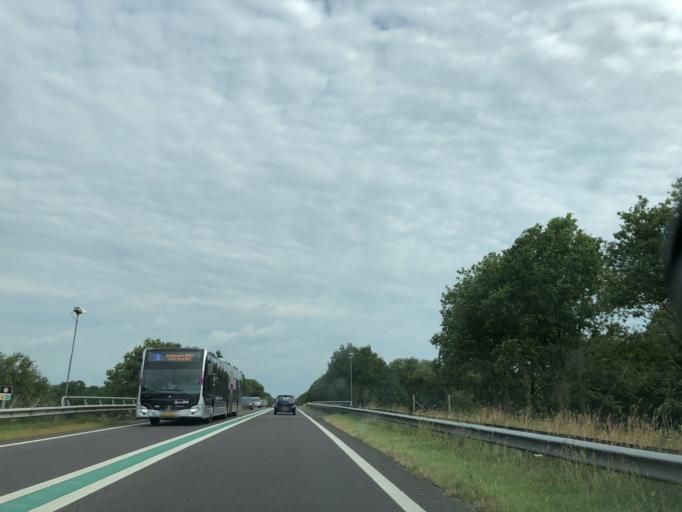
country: NL
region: Drenthe
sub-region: Gemeente Tynaarlo
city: Tynaarlo
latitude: 53.1012
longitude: 6.6256
